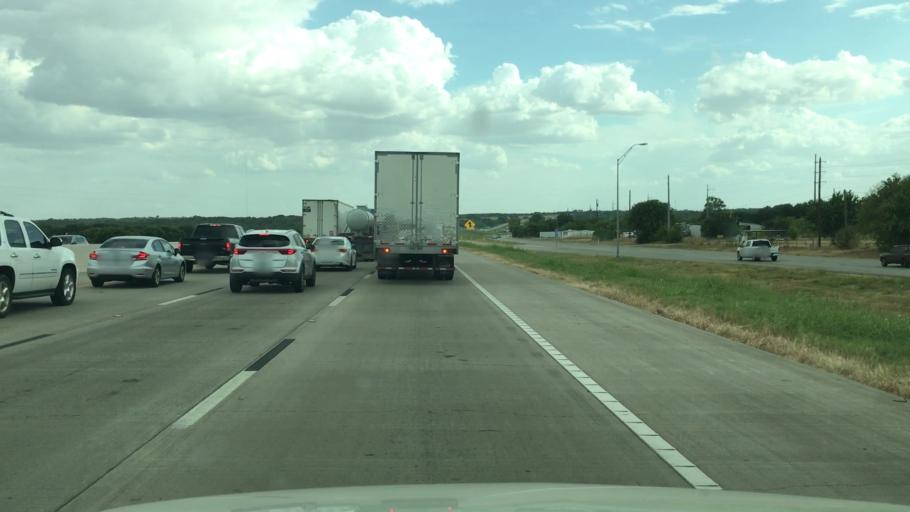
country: US
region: Texas
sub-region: McLennan County
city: Lorena
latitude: 31.3460
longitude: -97.2210
